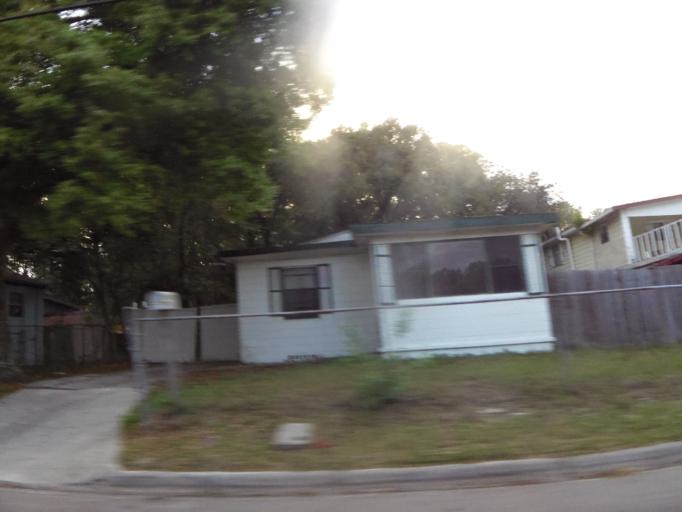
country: US
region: Florida
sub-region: Duval County
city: Jacksonville
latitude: 30.3604
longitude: -81.6371
